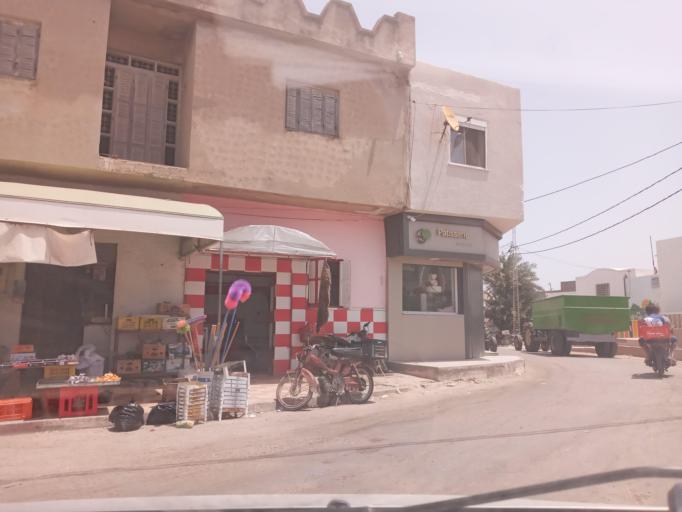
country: TN
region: Nabul
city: El Haouaria
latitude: 37.0116
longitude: 10.9540
